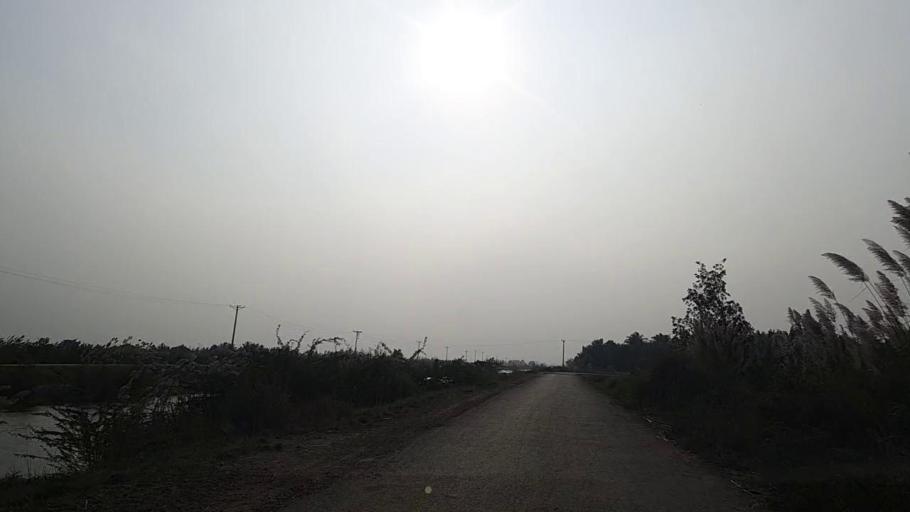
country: PK
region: Sindh
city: Mirpur Sakro
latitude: 24.6235
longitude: 67.5611
